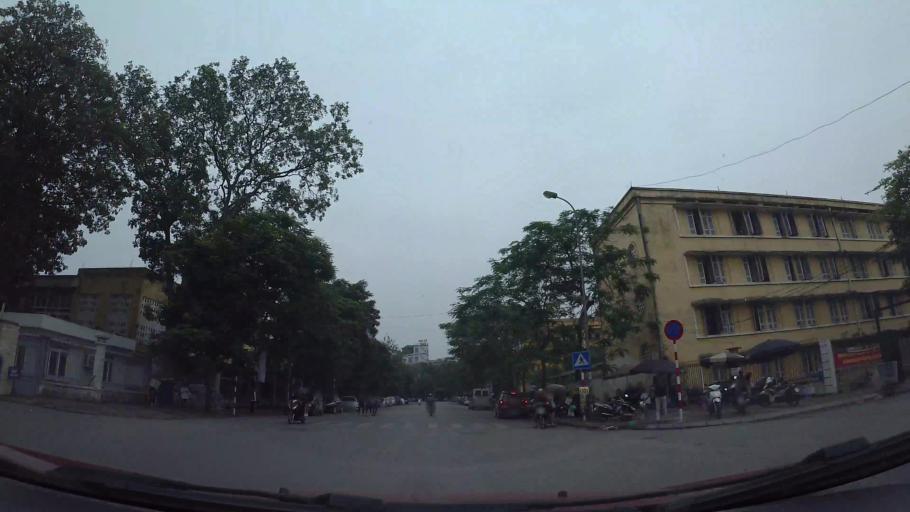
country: VN
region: Ha Noi
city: Hai BaTrung
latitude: 21.0051
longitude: 105.8457
